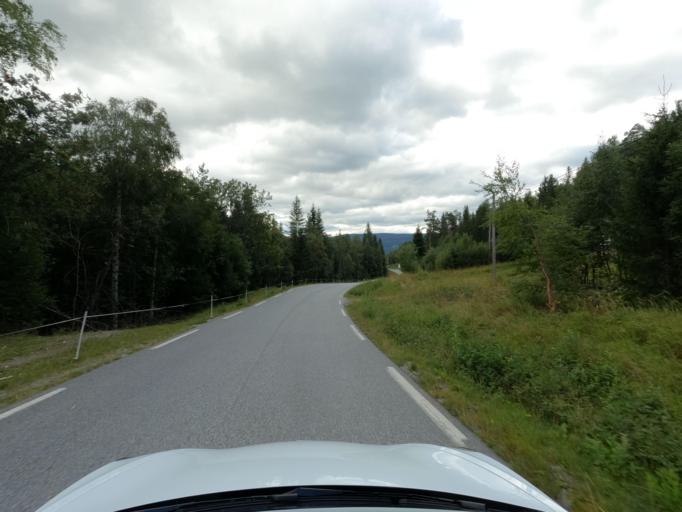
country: NO
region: Telemark
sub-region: Tinn
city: Rjukan
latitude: 60.0244
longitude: 8.7396
